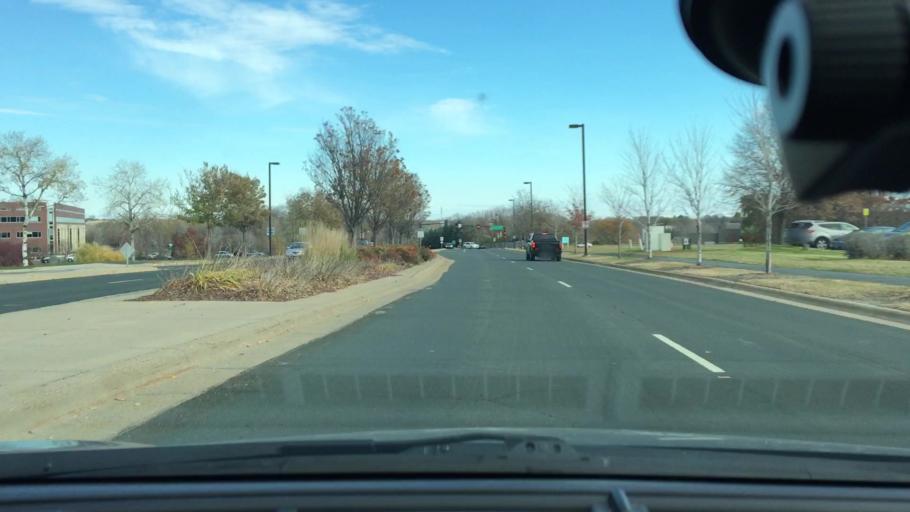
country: US
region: Minnesota
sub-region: Hennepin County
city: Maple Grove
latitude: 45.1025
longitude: -93.4707
